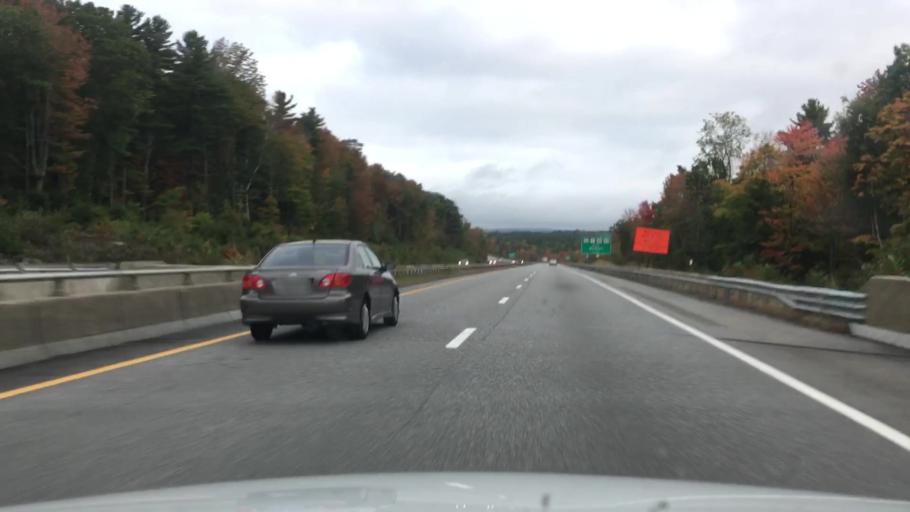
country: US
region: Maine
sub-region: Cumberland County
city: Cumberland Center
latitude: 43.8617
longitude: -70.3246
